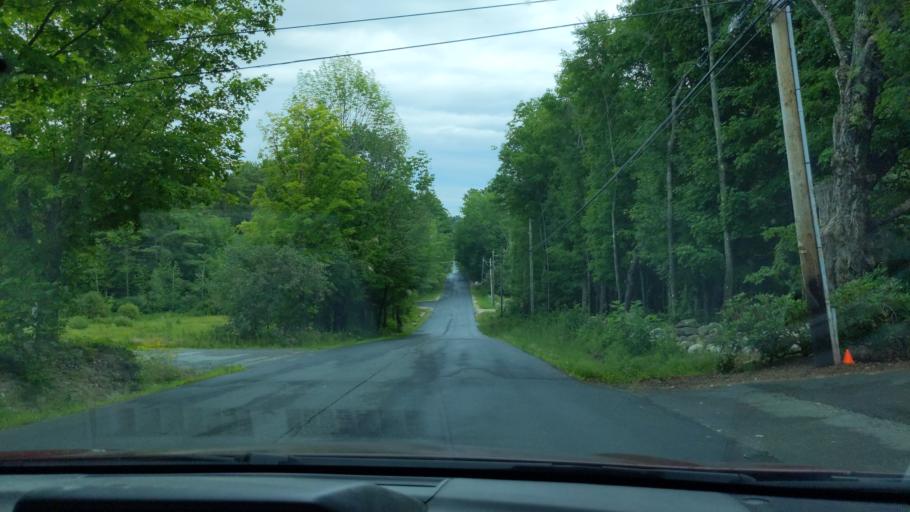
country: US
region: New Hampshire
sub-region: Merrimack County
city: New London
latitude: 43.4174
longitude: -72.0178
